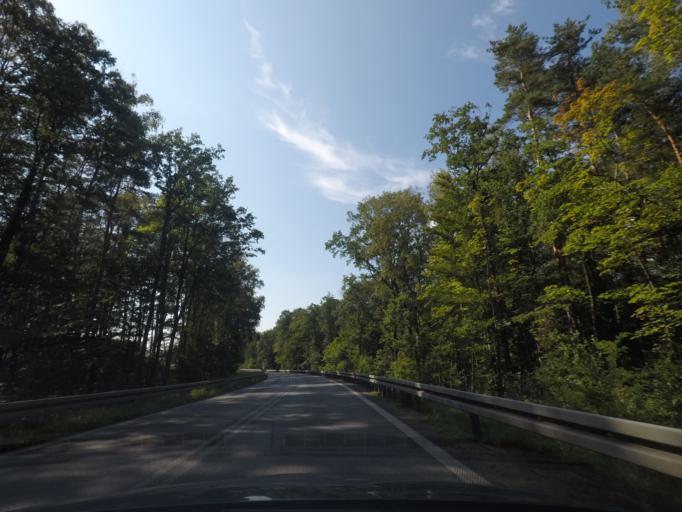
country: PL
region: Silesian Voivodeship
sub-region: Powiat pszczynski
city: Suszec
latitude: 50.0281
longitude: 18.8021
